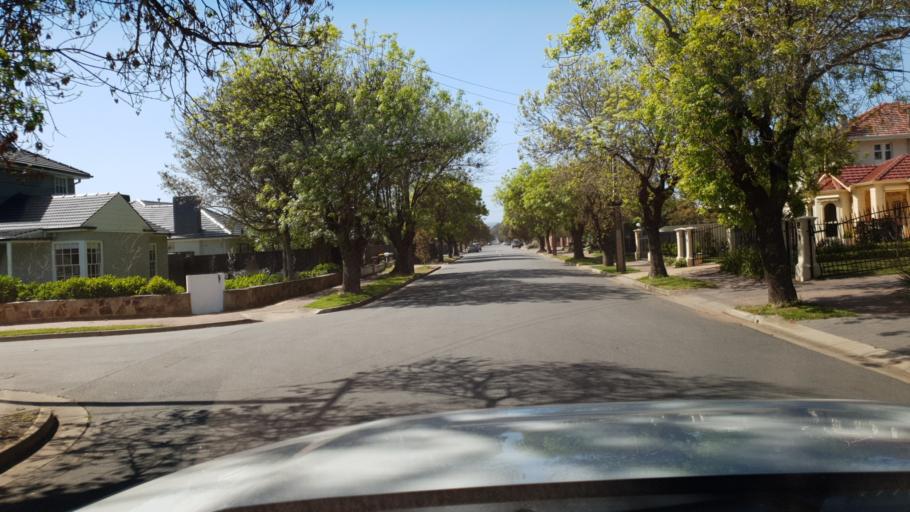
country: AU
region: South Australia
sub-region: Adelaide
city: Brighton
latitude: -35.0253
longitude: 138.5222
